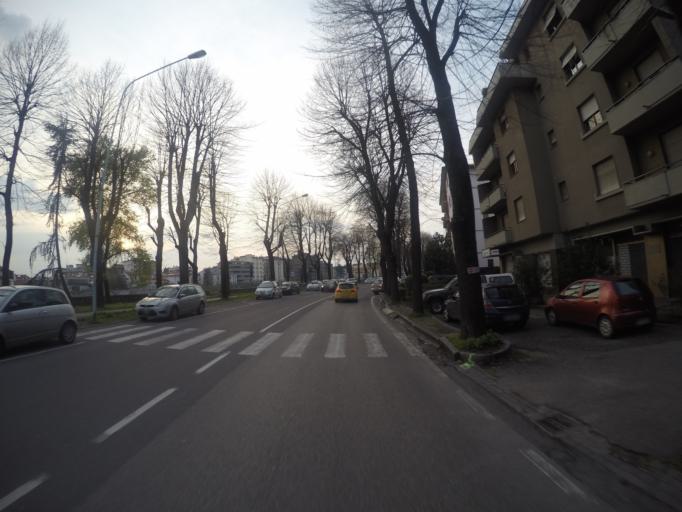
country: IT
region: Tuscany
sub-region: Provincia di Prato
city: Prato
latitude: 43.8738
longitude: 11.1107
